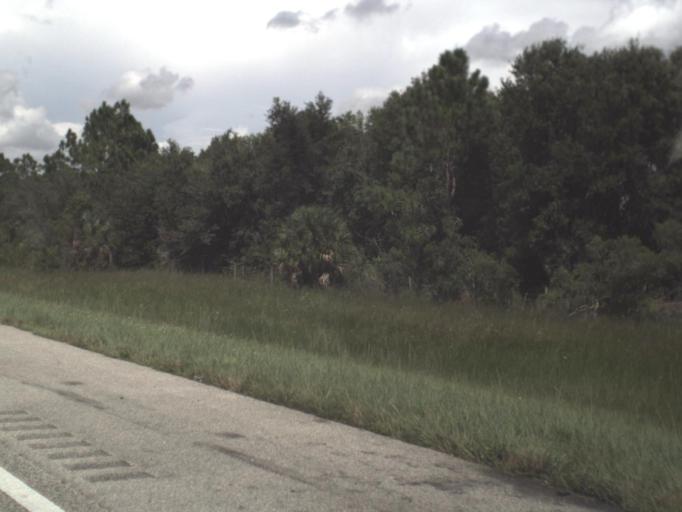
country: US
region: Florida
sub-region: Lee County
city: Suncoast Estates
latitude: 26.7919
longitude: -81.9053
